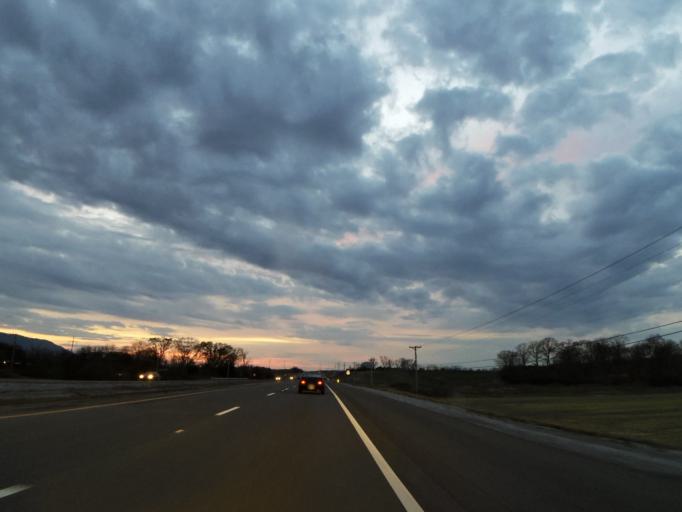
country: US
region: Tennessee
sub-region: Polk County
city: Benton
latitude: 35.2311
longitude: -84.5728
